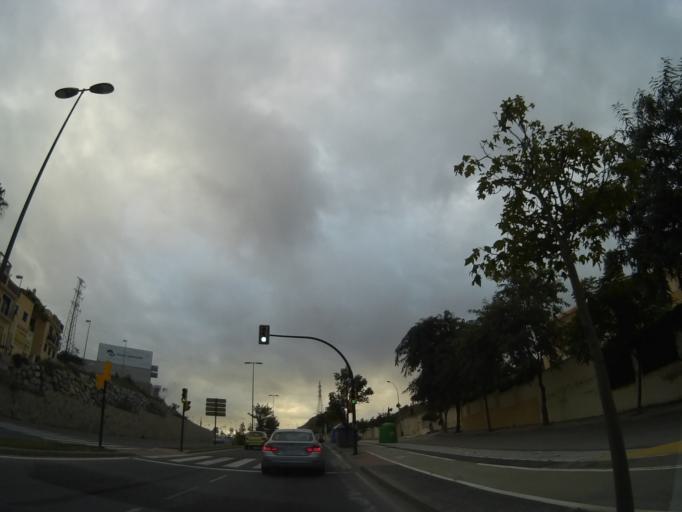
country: ES
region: Andalusia
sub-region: Provincia de Malaga
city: Malaga
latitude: 36.7082
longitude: -4.4882
